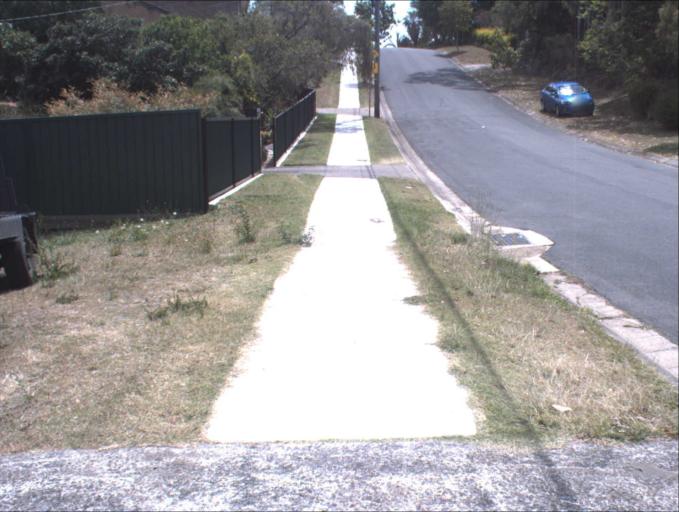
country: AU
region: Queensland
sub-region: Logan
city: Slacks Creek
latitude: -27.6525
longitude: 153.1788
